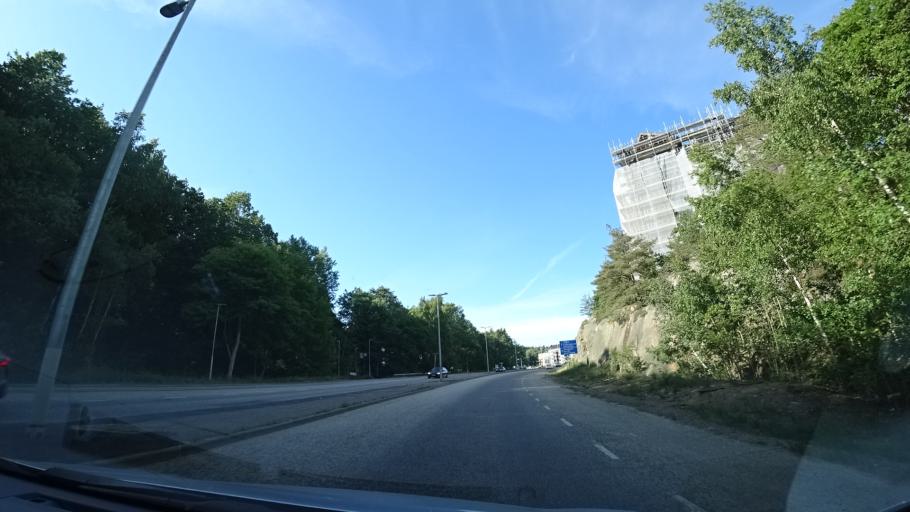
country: SE
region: Vaestra Goetaland
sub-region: Goteborg
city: Billdal
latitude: 57.5966
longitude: 11.9485
